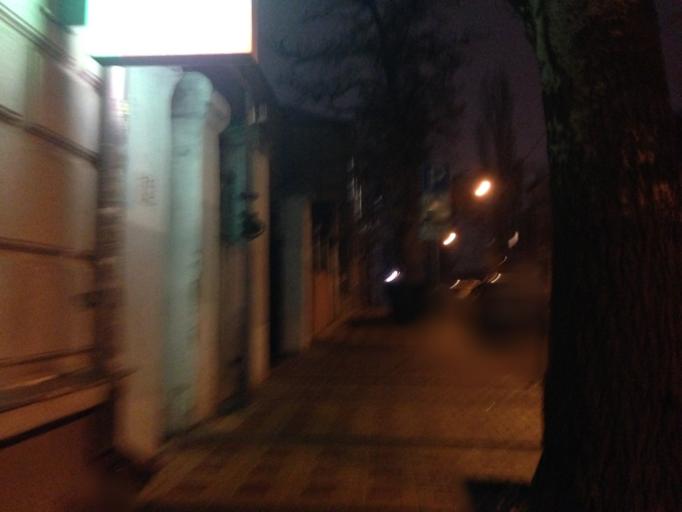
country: RU
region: Rostov
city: Rostov-na-Donu
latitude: 47.2242
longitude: 39.7148
